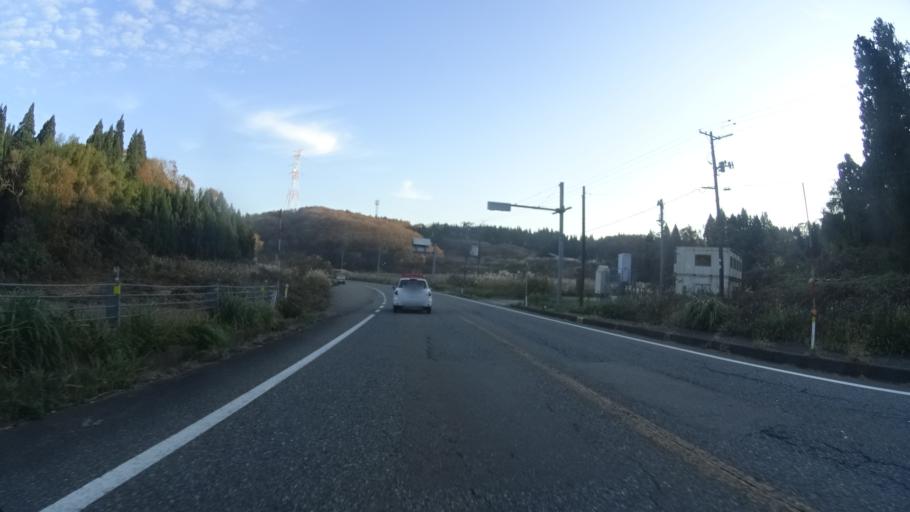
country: JP
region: Niigata
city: Kashiwazaki
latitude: 37.4079
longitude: 138.6867
